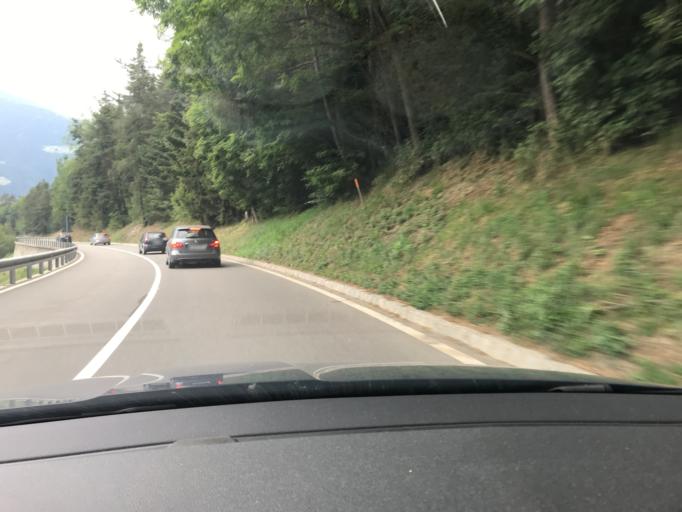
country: IT
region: Trentino-Alto Adige
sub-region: Bolzano
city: Bressanone
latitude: 46.6948
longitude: 11.6837
